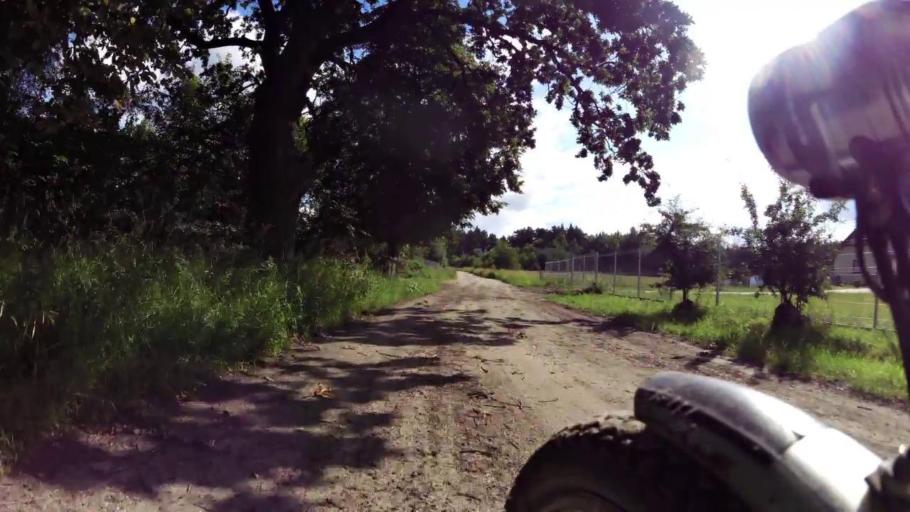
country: PL
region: West Pomeranian Voivodeship
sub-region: Powiat swidwinski
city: Swidwin
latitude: 53.7507
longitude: 15.8984
